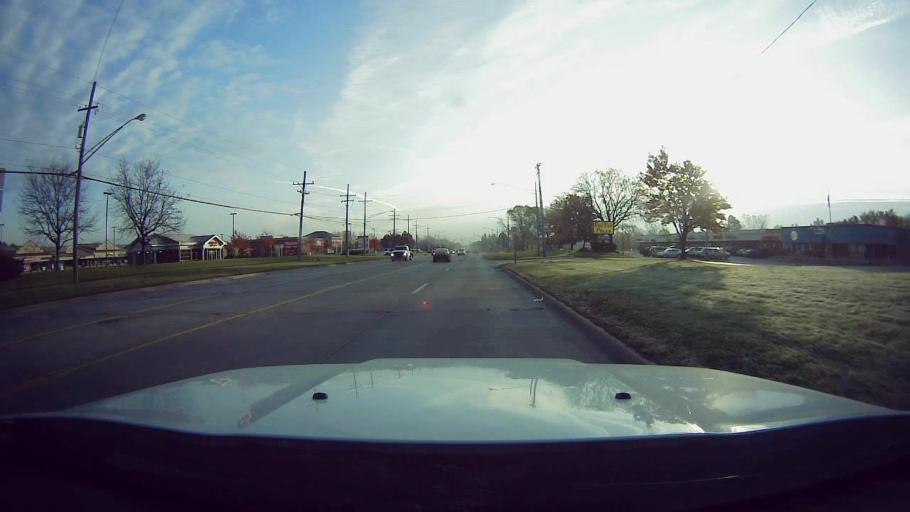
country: US
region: Michigan
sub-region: Macomb County
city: Fraser
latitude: 42.5521
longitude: -82.9923
